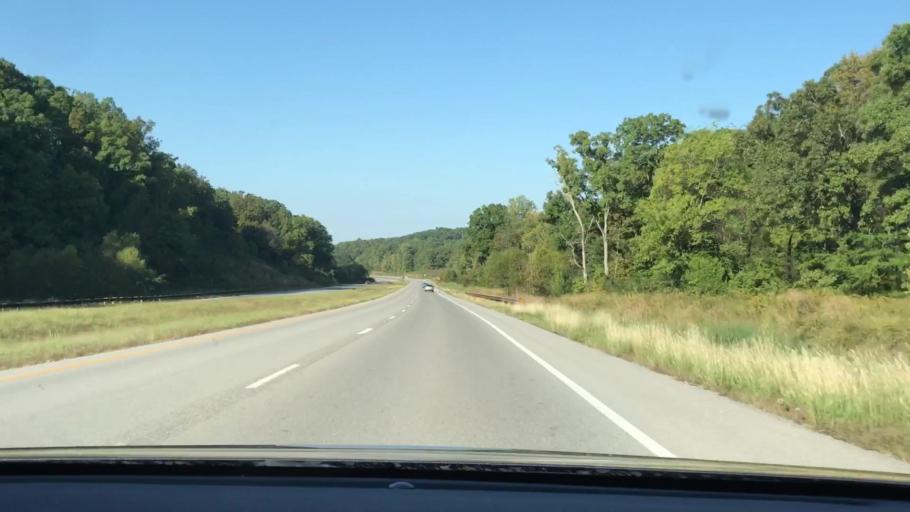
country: US
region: Kentucky
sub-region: Marshall County
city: Benton
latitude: 36.7794
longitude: -88.0917
